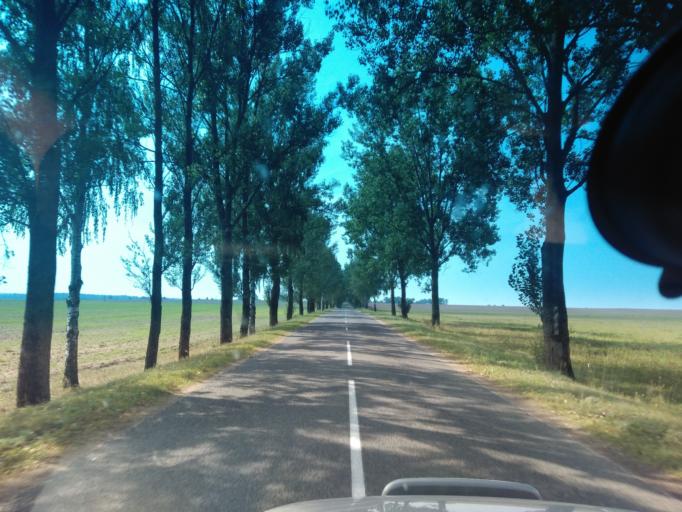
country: BY
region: Minsk
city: Kapyl'
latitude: 53.2704
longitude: 27.2028
